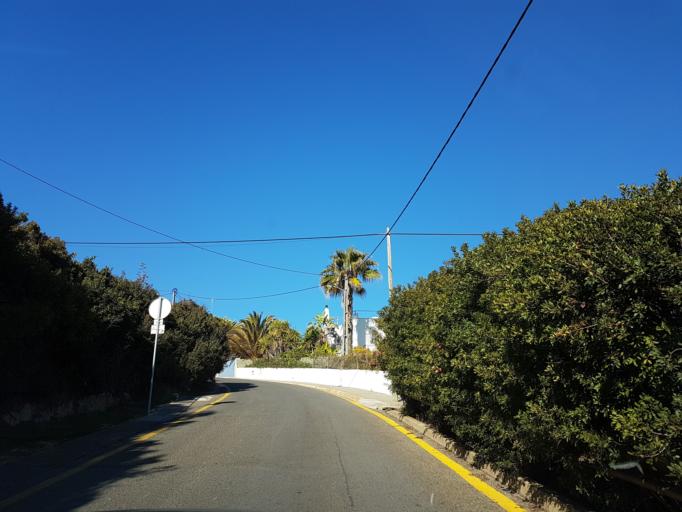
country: PT
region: Faro
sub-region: Lagoa
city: Carvoeiro
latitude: 37.0888
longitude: -8.4273
